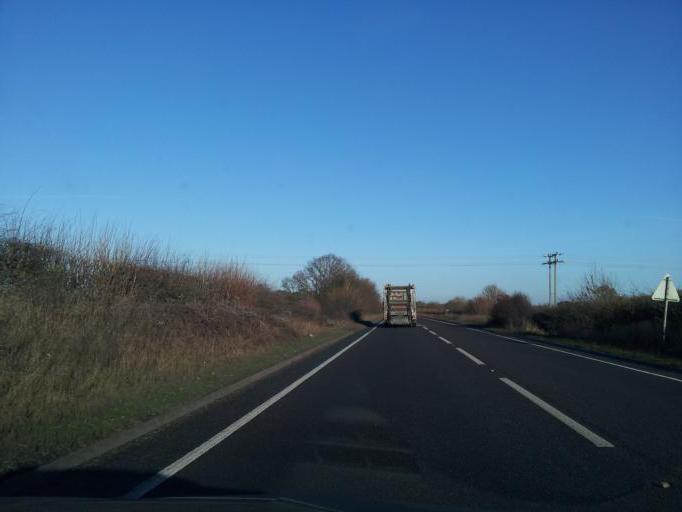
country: GB
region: England
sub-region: Suffolk
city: Long Melford
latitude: 52.0636
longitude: 0.7243
